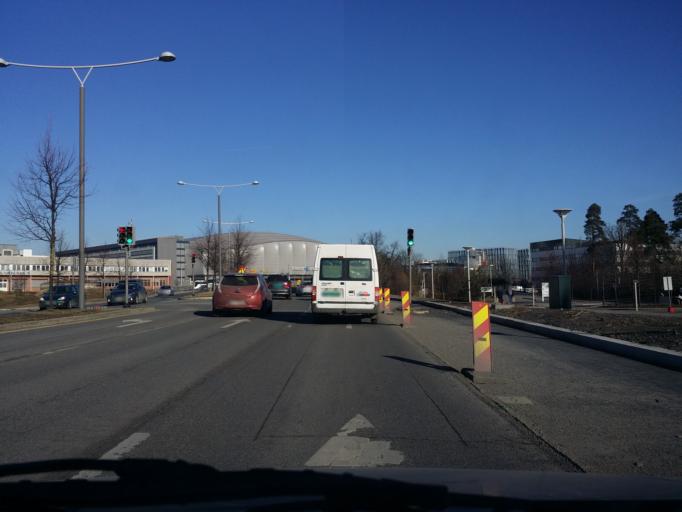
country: NO
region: Akershus
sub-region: Baerum
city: Lysaker
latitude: 59.8996
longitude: 10.6260
